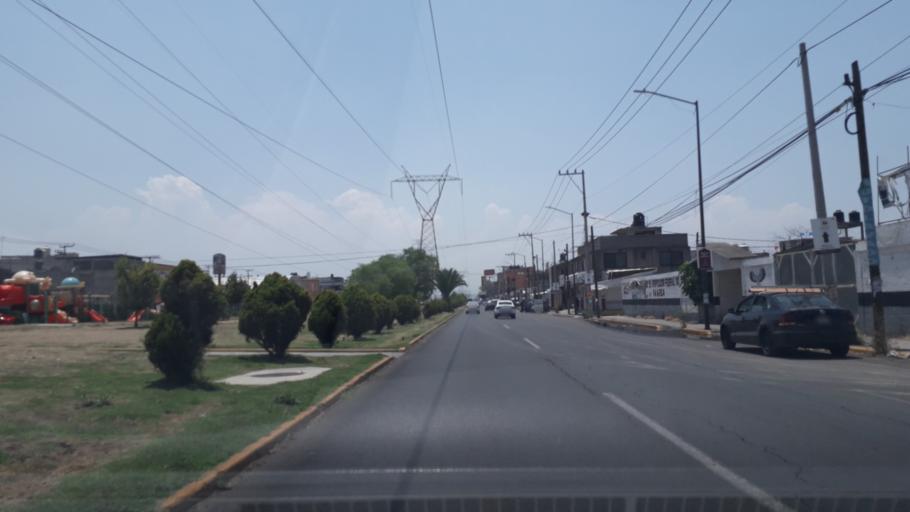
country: MX
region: Mexico
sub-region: Tultitlan
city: Fuentes del Valle
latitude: 19.6411
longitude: -99.1305
